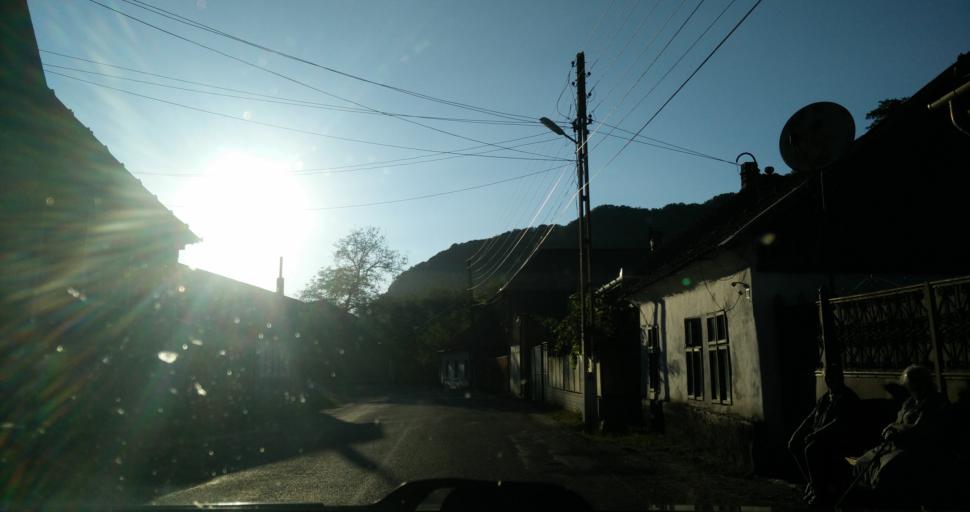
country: RO
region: Bihor
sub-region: Oras Nucet
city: Nucet
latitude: 46.4814
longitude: 22.5860
